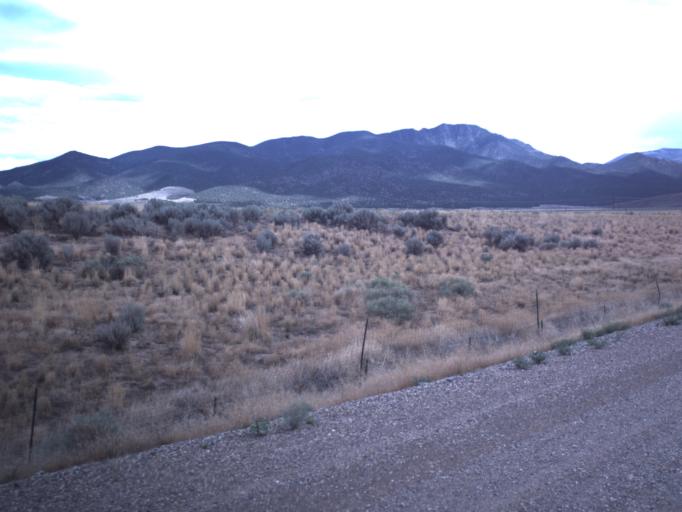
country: US
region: Utah
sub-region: Beaver County
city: Beaver
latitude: 38.0713
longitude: -112.6906
